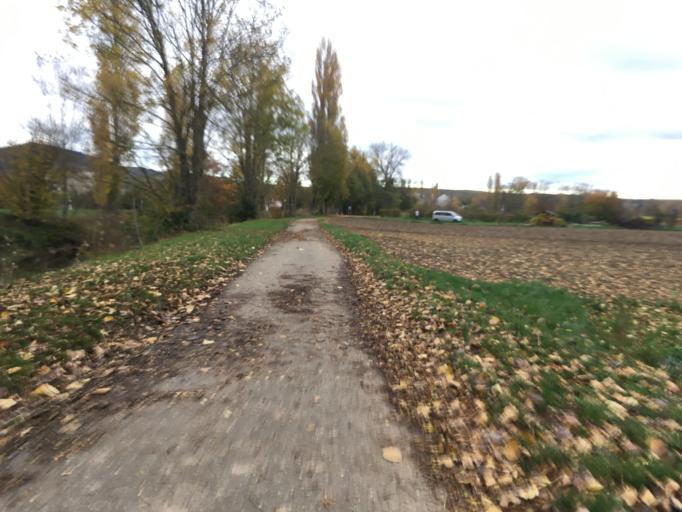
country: DE
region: Baden-Wuerttemberg
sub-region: Freiburg Region
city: Botzingen
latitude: 48.0651
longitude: 7.7246
